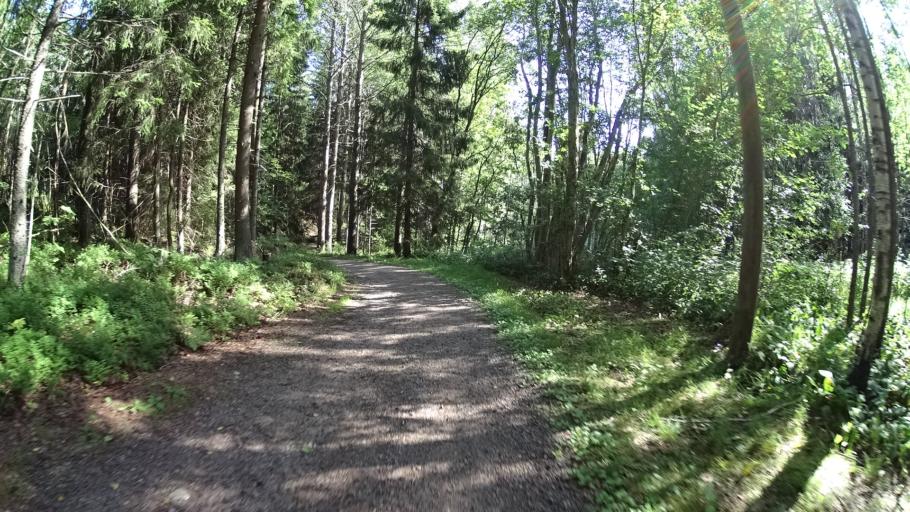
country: FI
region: Uusimaa
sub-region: Helsinki
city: Espoo
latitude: 60.2311
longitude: 24.6537
